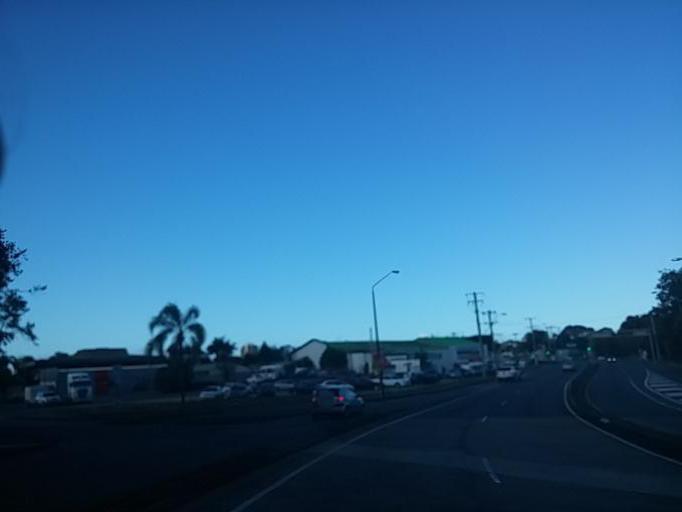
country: AU
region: New South Wales
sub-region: Tweed
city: Tweed Heads West
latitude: -28.1813
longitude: 153.5379
